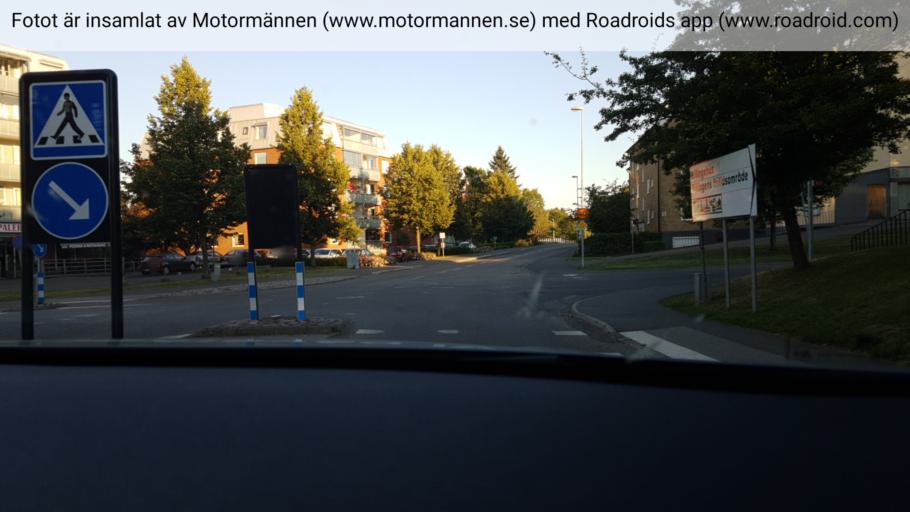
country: SE
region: Vaestra Goetaland
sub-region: Skovde Kommun
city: Skoevde
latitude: 58.3953
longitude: 13.8333
